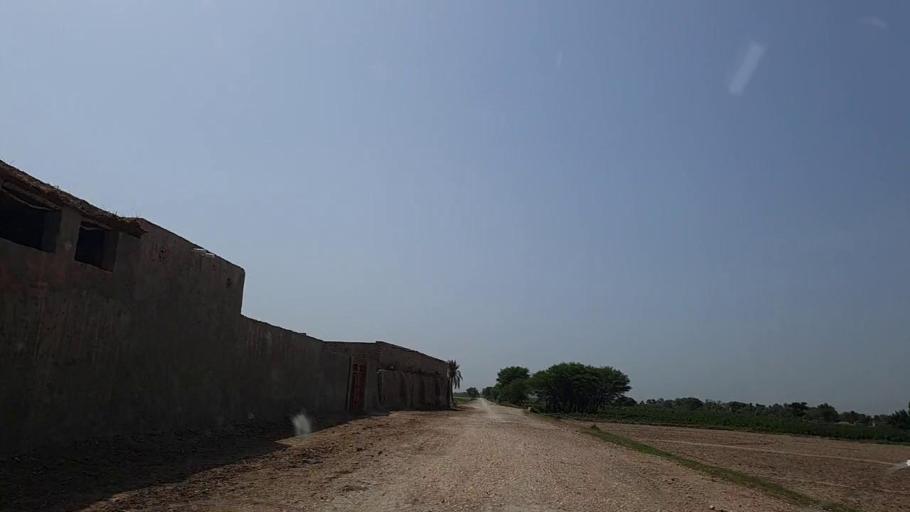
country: PK
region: Sindh
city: Naushahro Firoz
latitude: 26.8498
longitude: 68.0106
